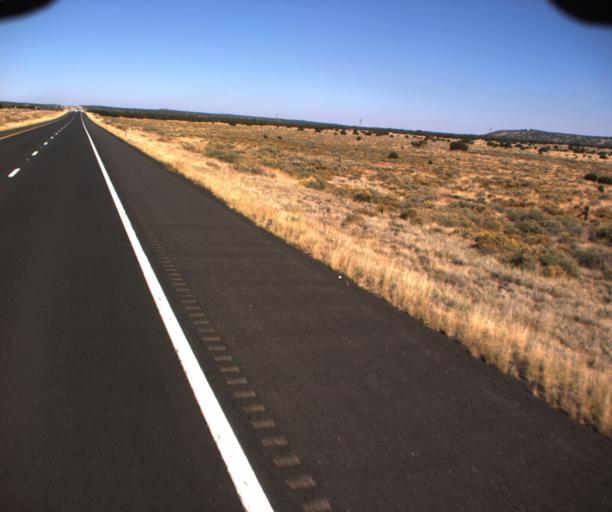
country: US
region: Arizona
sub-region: Coconino County
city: Flagstaff
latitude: 35.4457
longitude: -111.5641
